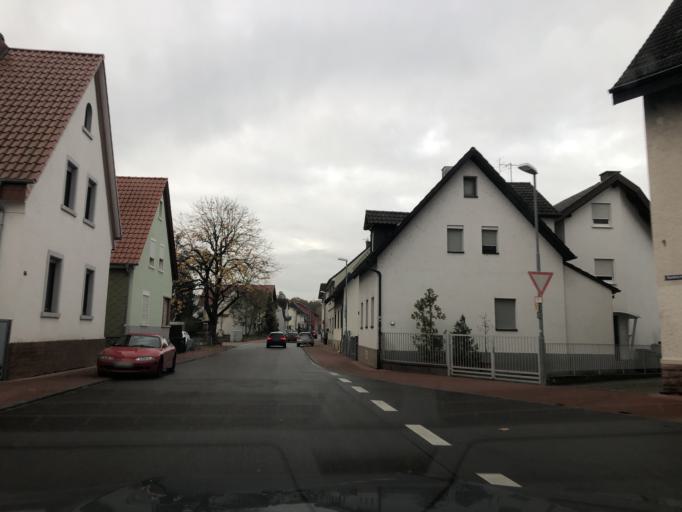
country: DE
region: Baden-Wuerttemberg
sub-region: Karlsruhe Region
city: Sandhausen
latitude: 49.3375
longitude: 8.6553
